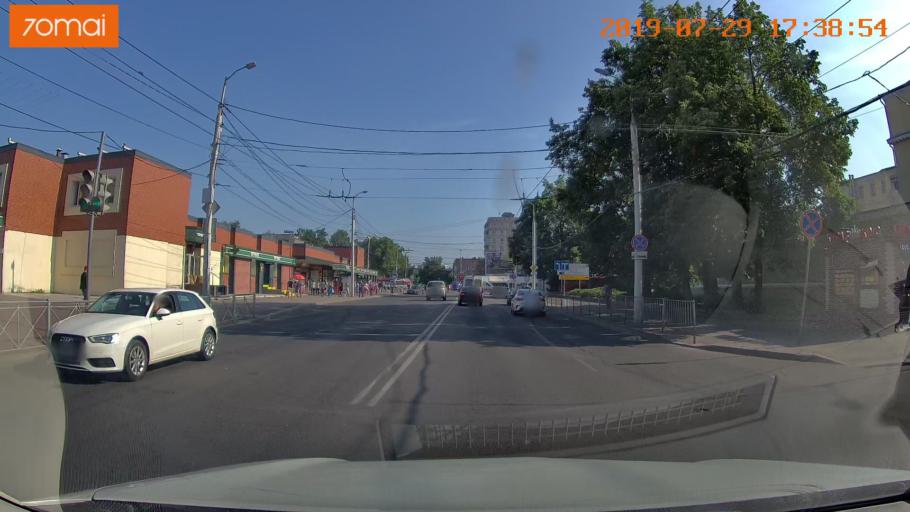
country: RU
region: Kaliningrad
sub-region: Gorod Kaliningrad
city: Kaliningrad
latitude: 54.7208
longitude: 20.5075
